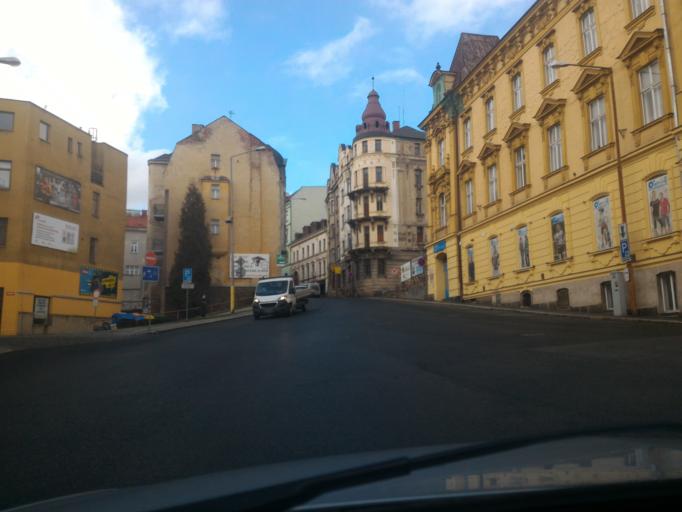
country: CZ
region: Liberecky
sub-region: Okres Jablonec nad Nisou
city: Jablonec nad Nisou
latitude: 50.7243
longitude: 15.1749
